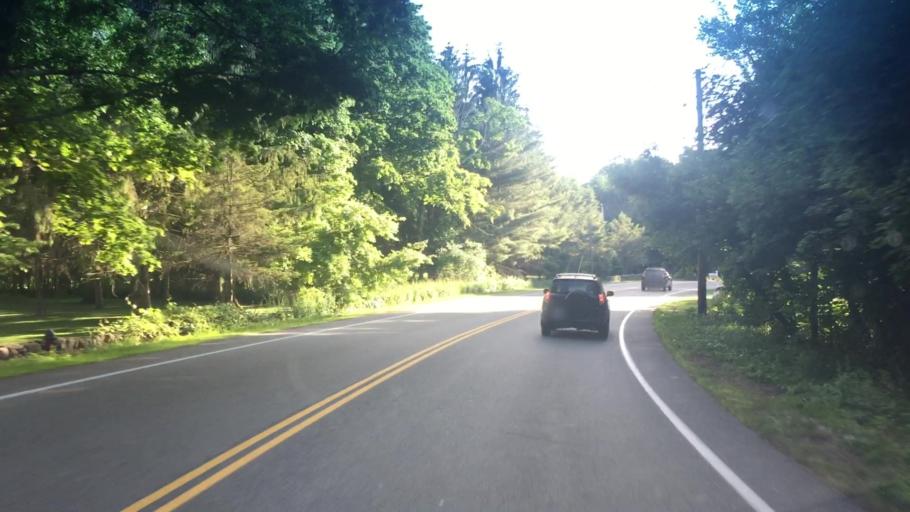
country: US
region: Massachusetts
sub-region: Norfolk County
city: Medfield
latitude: 42.2011
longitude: -71.2674
